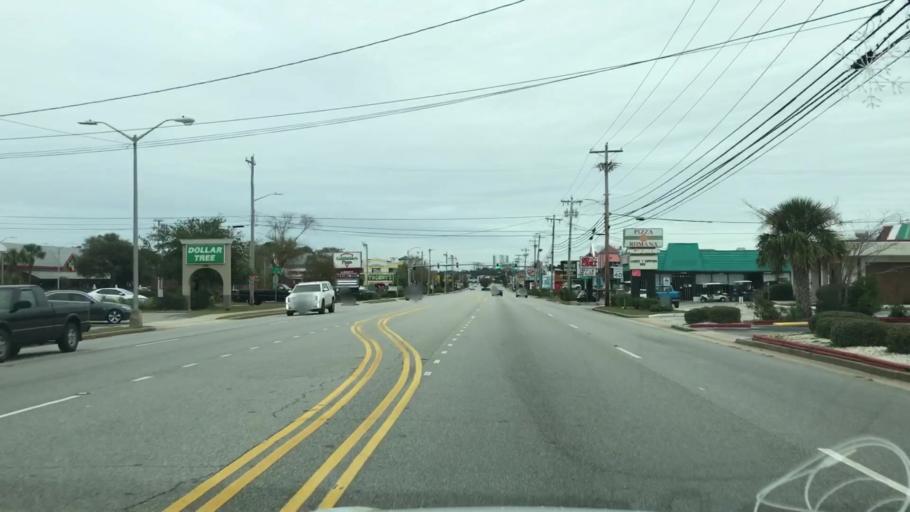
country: US
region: South Carolina
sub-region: Horry County
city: Myrtle Beach
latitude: 33.6808
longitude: -78.8968
